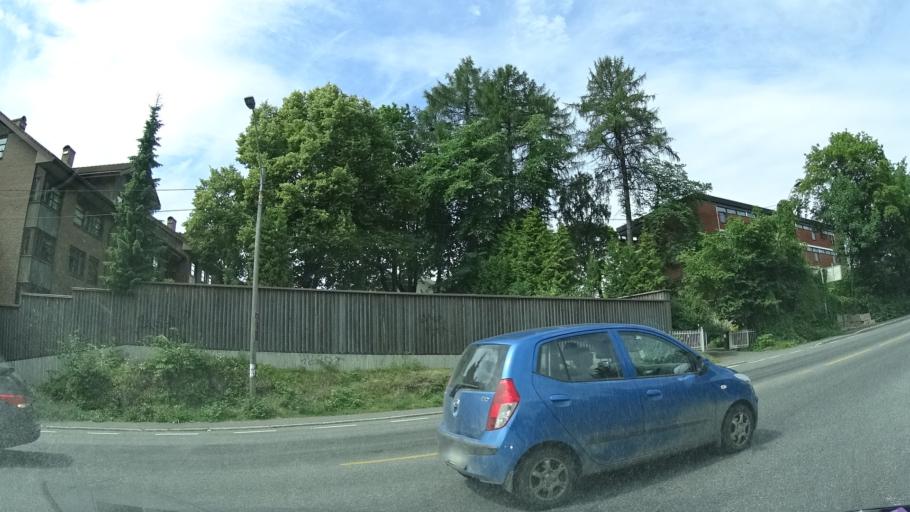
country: NO
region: Oslo
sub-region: Oslo
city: Oslo
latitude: 59.9524
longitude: 10.7612
